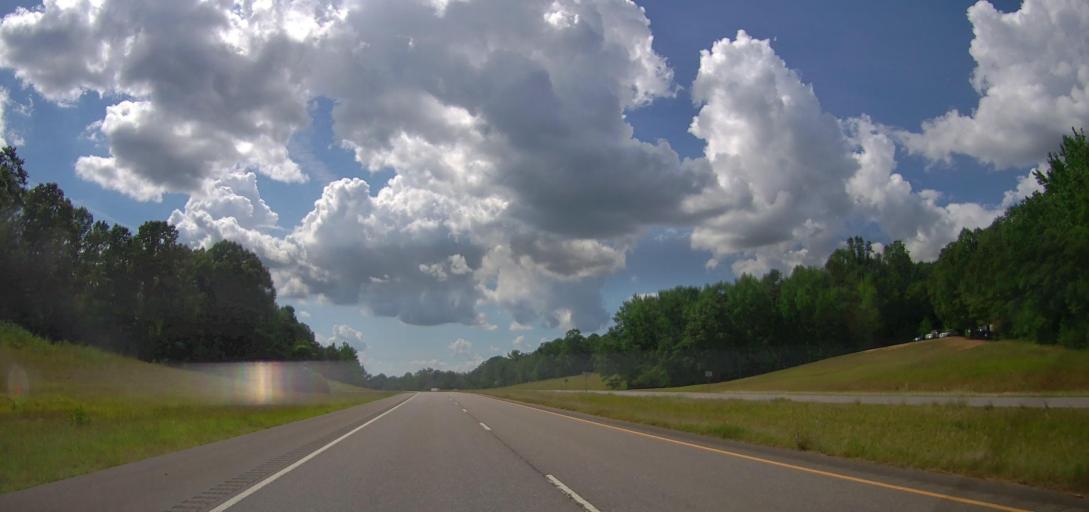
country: US
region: Alabama
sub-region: Pickens County
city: Reform
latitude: 33.4025
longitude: -88.0718
